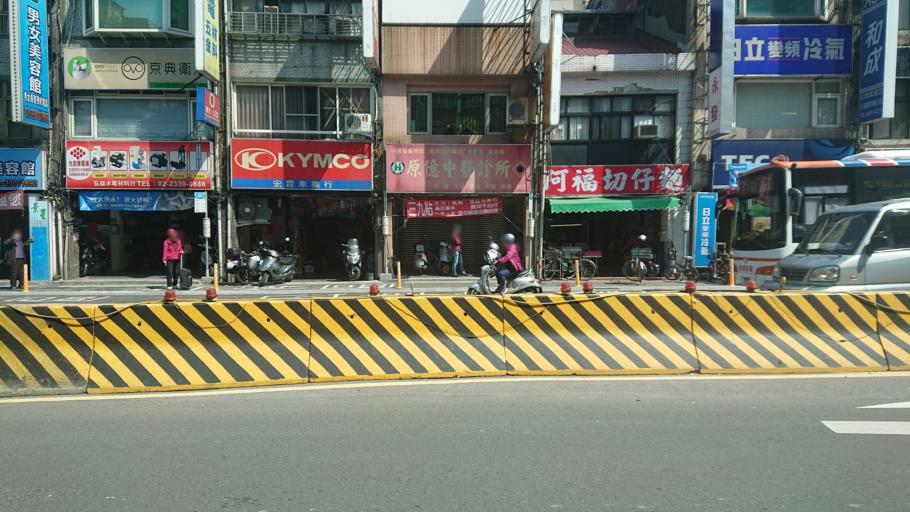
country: TW
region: Taipei
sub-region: Taipei
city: Banqiao
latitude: 25.0250
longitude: 121.5004
